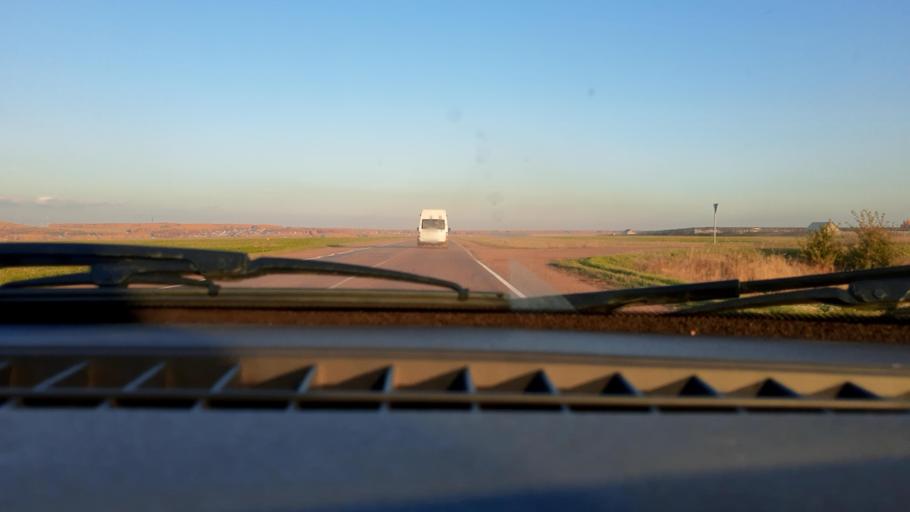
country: RU
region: Bashkortostan
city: Asanovo
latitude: 54.8248
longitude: 55.6450
